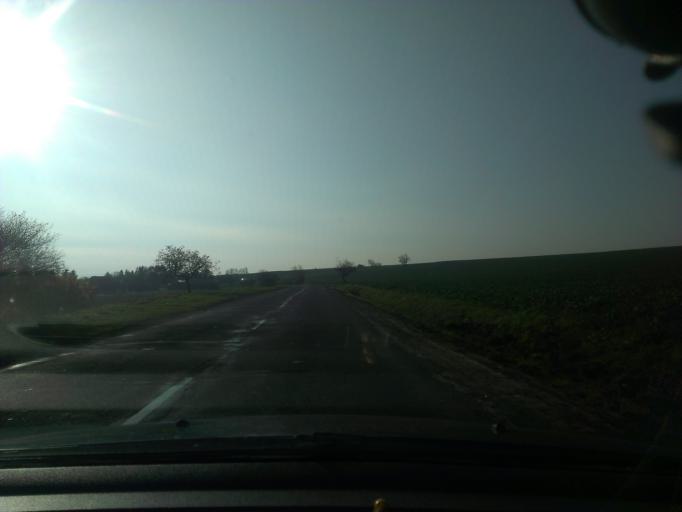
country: SK
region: Trnavsky
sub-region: Okres Trnava
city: Piestany
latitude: 48.5311
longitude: 17.9602
